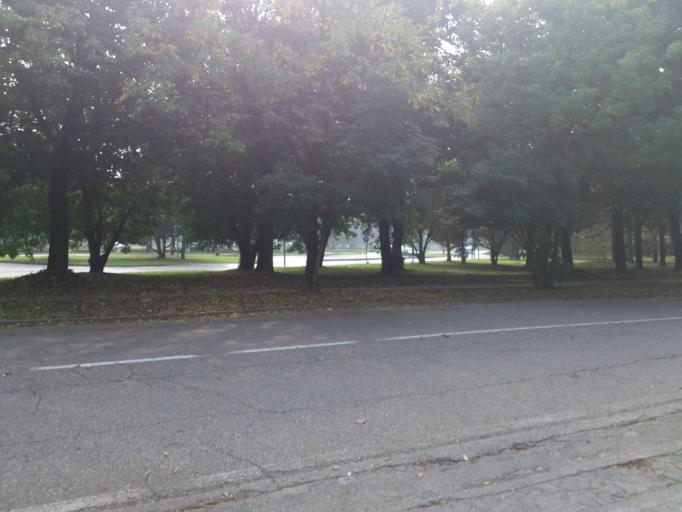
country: IT
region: Lombardy
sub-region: Citta metropolitana di Milano
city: San Donato Milanese
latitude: 45.4187
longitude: 9.2818
